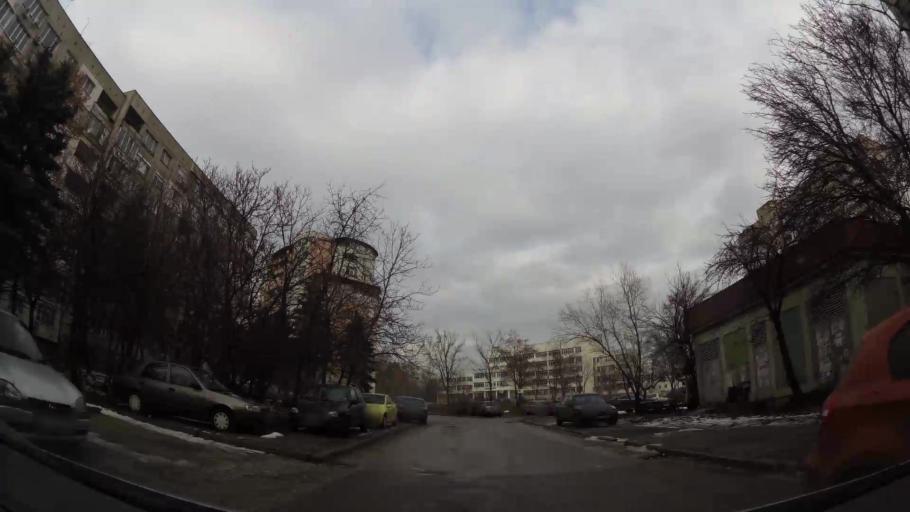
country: BG
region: Sofiya
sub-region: Obshtina Bozhurishte
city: Bozhurishte
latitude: 42.7098
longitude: 23.2523
